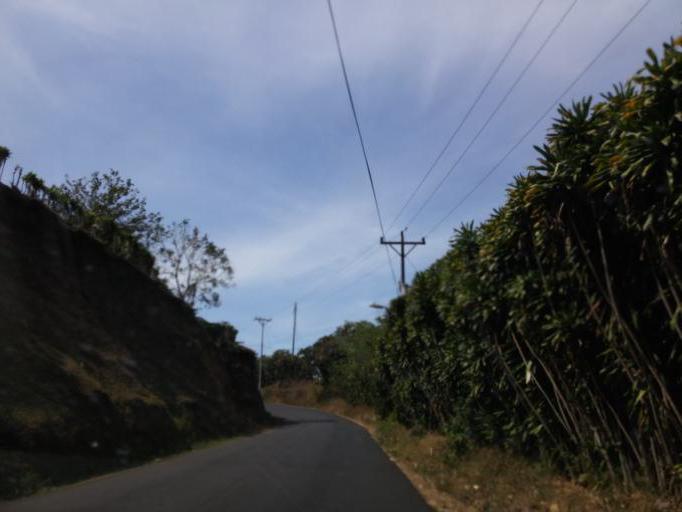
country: CR
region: Alajuela
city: Sabanilla
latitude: 10.0641
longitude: -84.2066
